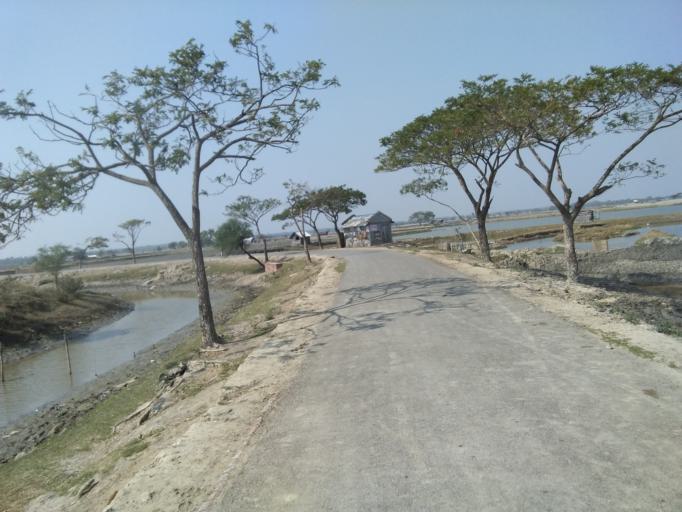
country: IN
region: West Bengal
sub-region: North 24 Parganas
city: Taki
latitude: 22.6339
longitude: 89.0133
